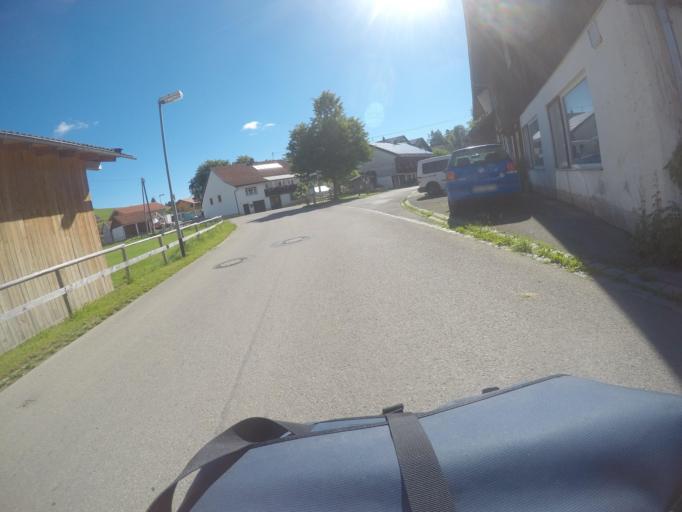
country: DE
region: Bavaria
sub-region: Swabia
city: Pfronten
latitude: 47.6058
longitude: 10.5607
